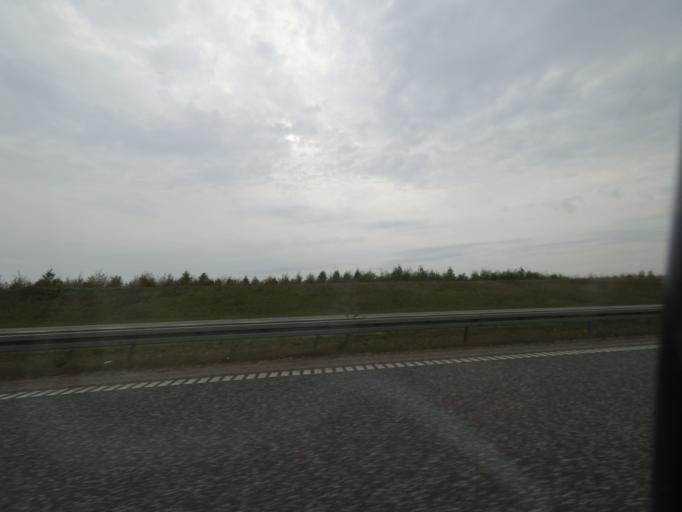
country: DK
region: South Denmark
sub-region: Faaborg-Midtfyn Kommune
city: Ringe
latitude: 55.2528
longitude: 10.4736
